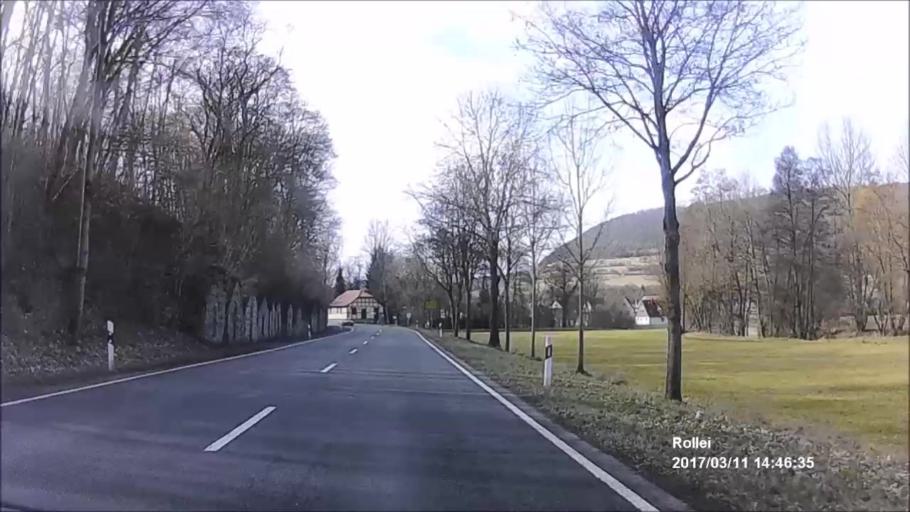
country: DE
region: Thuringia
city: Belrieth
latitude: 50.5273
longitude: 10.5015
